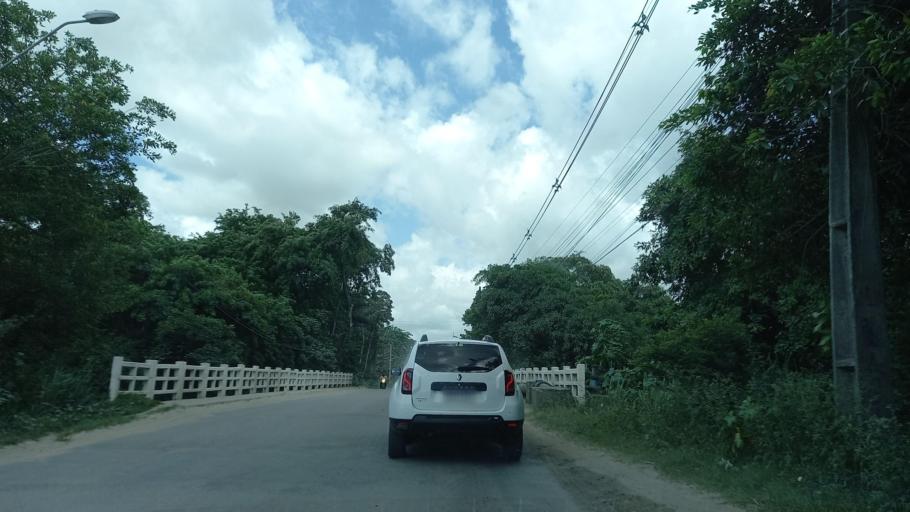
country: BR
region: Pernambuco
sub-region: Jaboatao Dos Guararapes
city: Jaboatao
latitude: -8.1585
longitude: -34.9754
